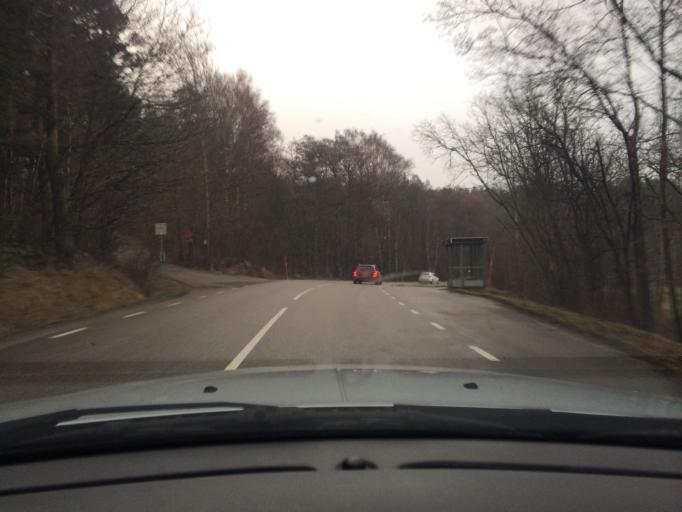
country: SE
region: Vaestra Goetaland
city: Svanesund
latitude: 58.1160
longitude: 11.8547
